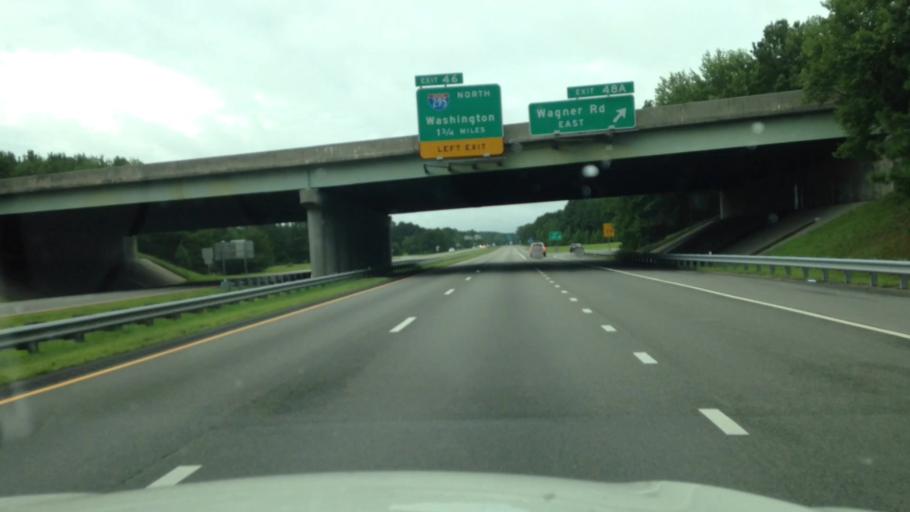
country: US
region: Virginia
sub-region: City of Petersburg
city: Petersburg
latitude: 37.1914
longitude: -77.3590
